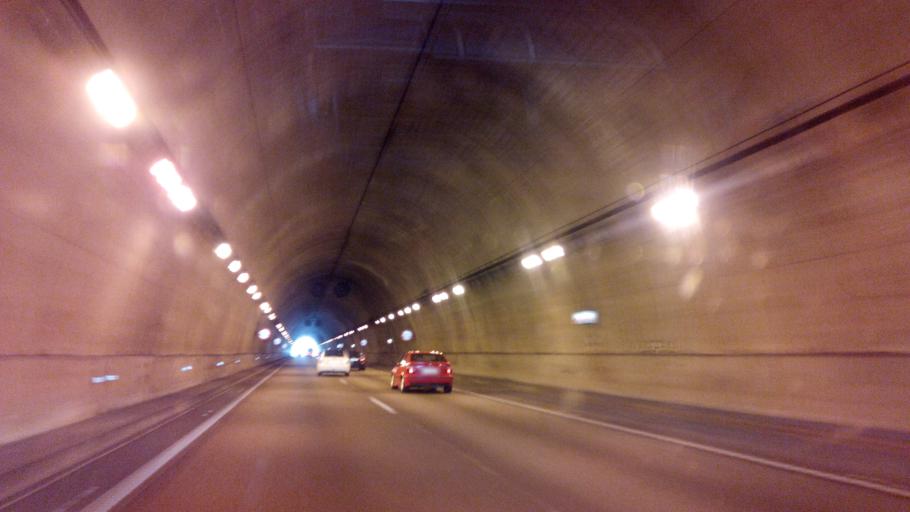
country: ES
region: Galicia
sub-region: Provincia de Pontevedra
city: Vigo
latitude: 42.2540
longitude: -8.6774
